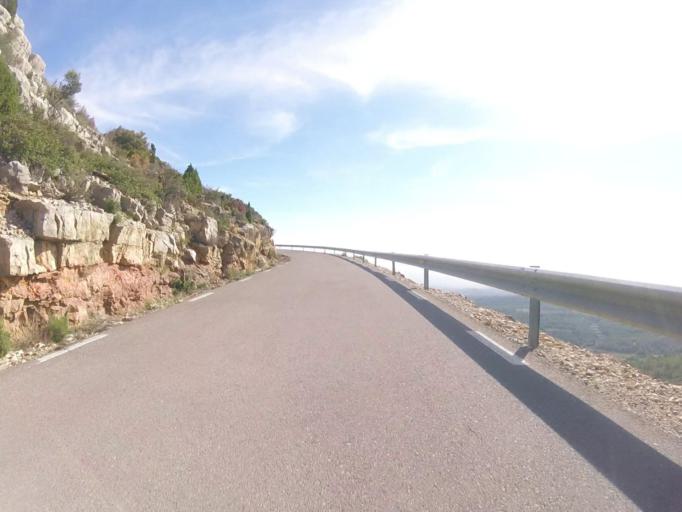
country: ES
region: Valencia
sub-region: Provincia de Castello
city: Sarratella
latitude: 40.2843
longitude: 0.0382
